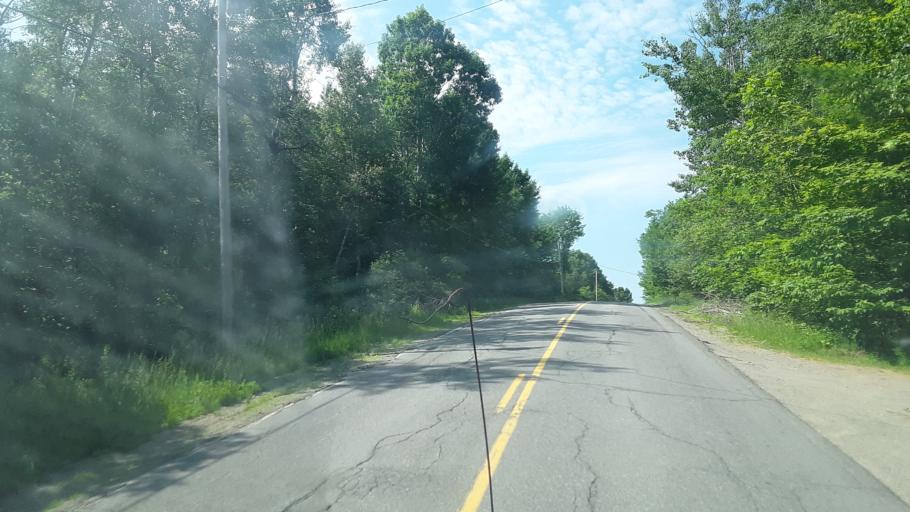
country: US
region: Maine
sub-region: Waldo County
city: Swanville
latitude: 44.5745
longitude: -68.9497
